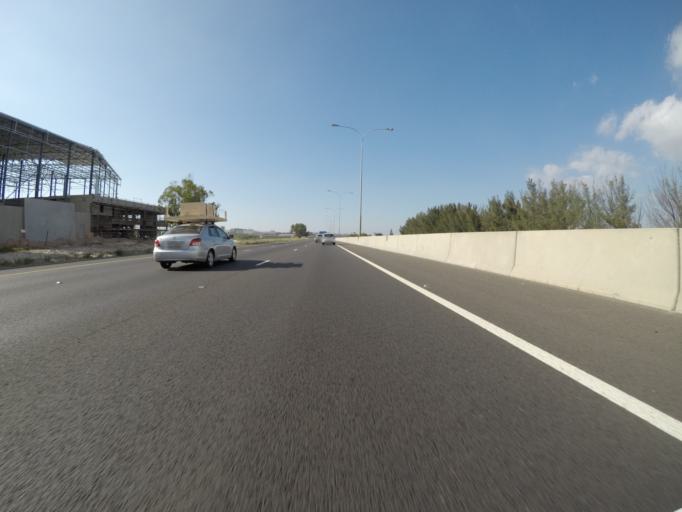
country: ZA
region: Western Cape
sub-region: City of Cape Town
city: Kraaifontein
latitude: -33.9267
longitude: 18.6630
